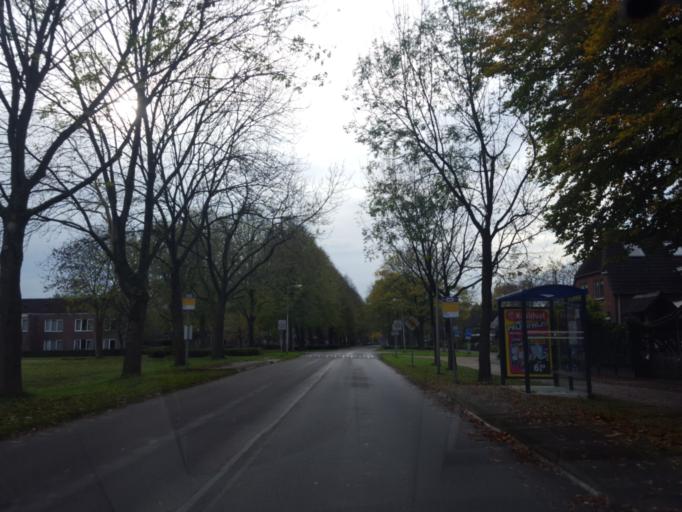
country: NL
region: Drenthe
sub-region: Gemeente Coevorden
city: Dalen
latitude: 52.7038
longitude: 6.7555
